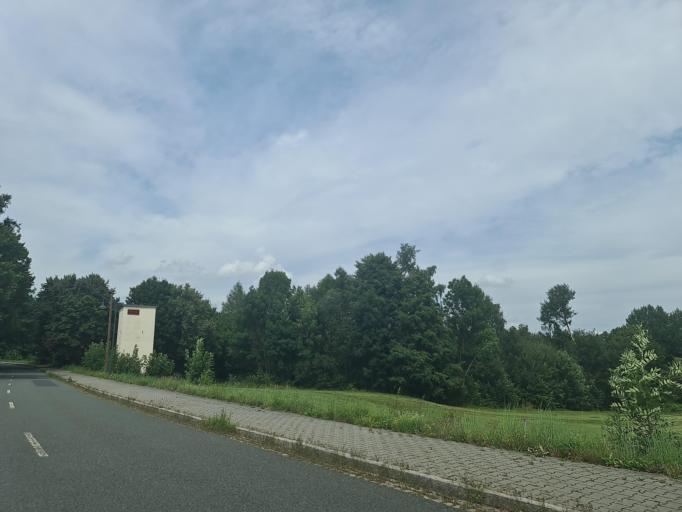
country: DE
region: Saxony
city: Hirschfeld
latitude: 50.6272
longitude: 12.4446
